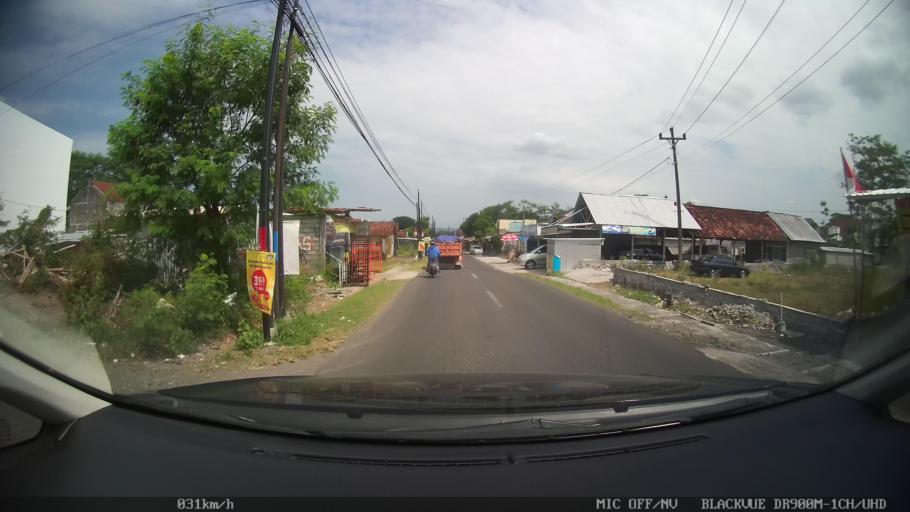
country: ID
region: Daerah Istimewa Yogyakarta
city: Depok
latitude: -7.7354
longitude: 110.4515
